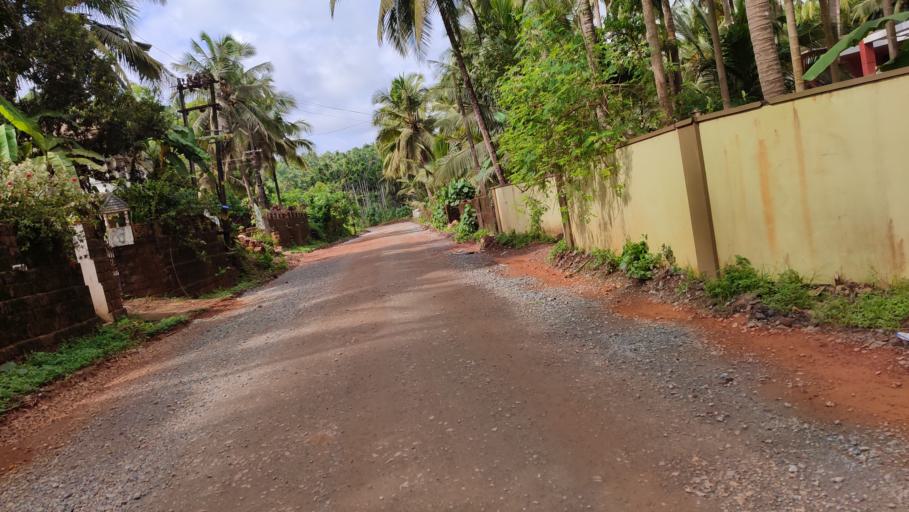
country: IN
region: Kerala
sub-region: Kasaragod District
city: Kasaragod
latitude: 12.5188
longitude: 75.0718
